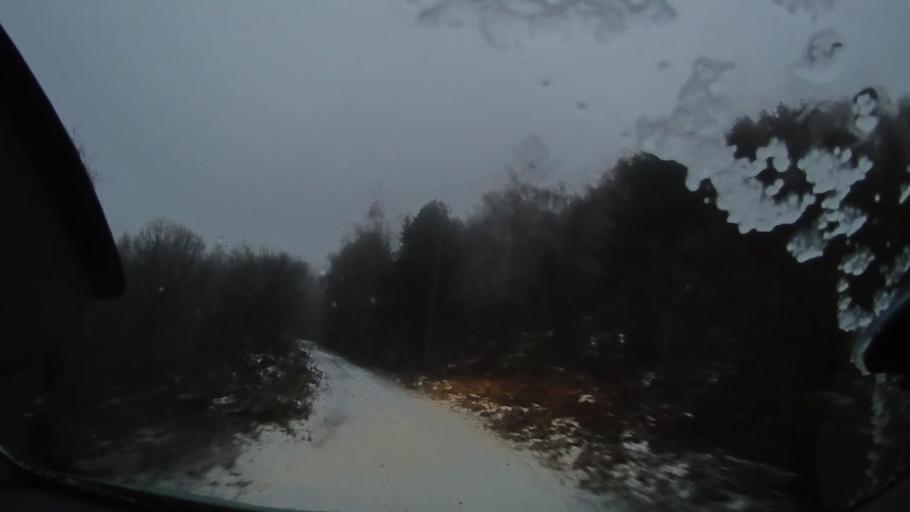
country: RO
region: Alba
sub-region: Comuna Avram Iancu
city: Avram Iancu
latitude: 46.3097
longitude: 22.8000
